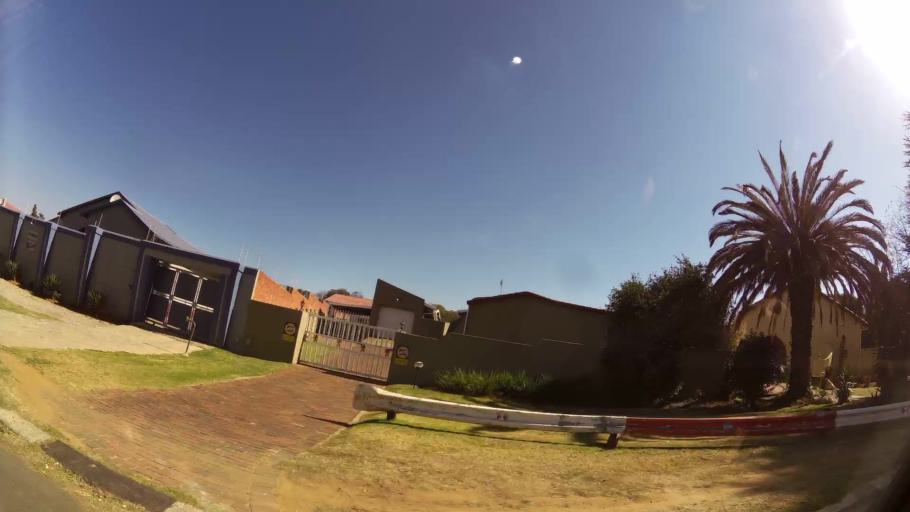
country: ZA
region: Gauteng
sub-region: City of Johannesburg Metropolitan Municipality
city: Johannesburg
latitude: -26.2647
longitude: 27.9952
